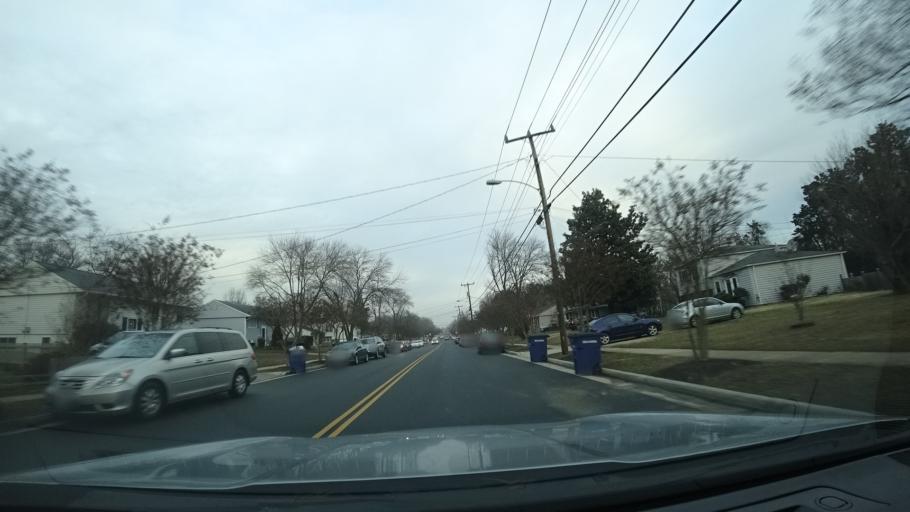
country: US
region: Virginia
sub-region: Fairfax County
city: Herndon
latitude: 38.9627
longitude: -77.3912
